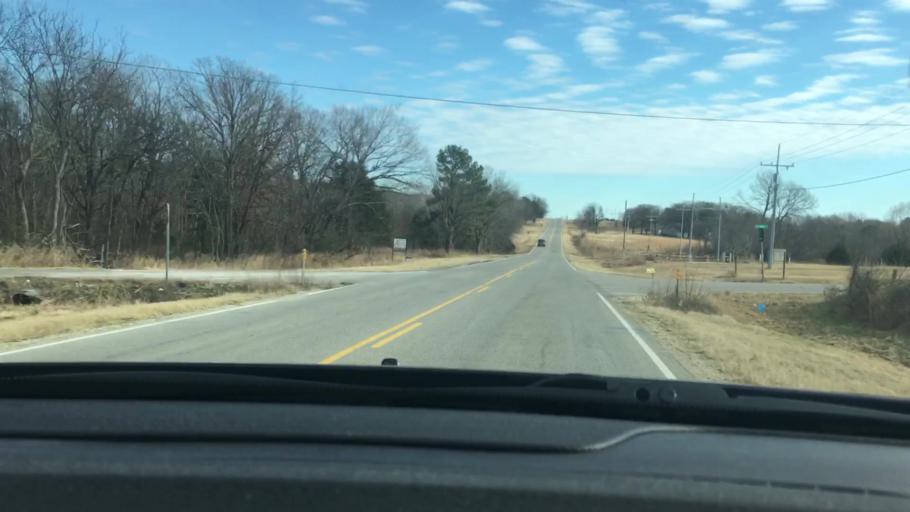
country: US
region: Oklahoma
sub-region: Pontotoc County
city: Ada
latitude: 34.7860
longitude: -96.7928
